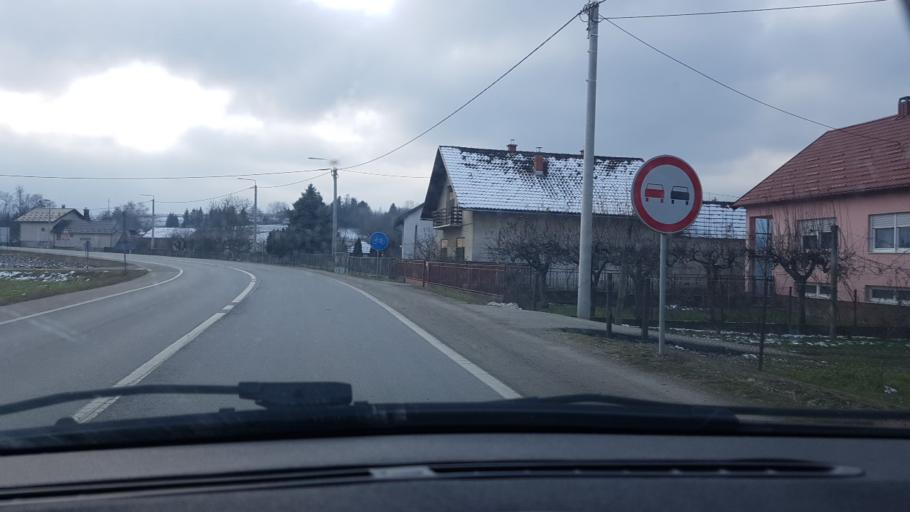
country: HR
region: Varazdinska
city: Tuzno
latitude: 46.2797
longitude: 16.2072
